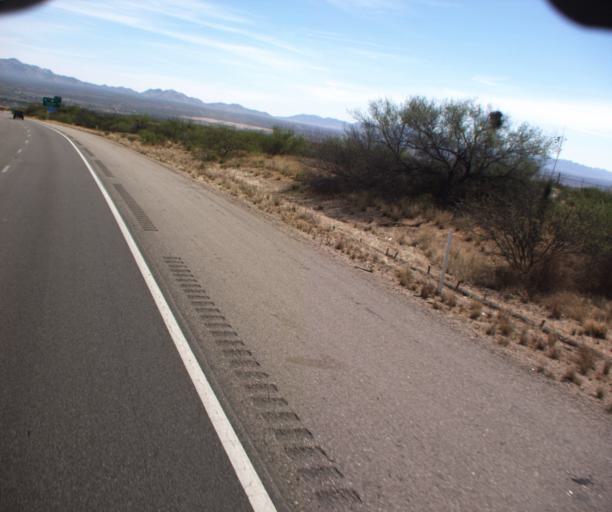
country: US
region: Arizona
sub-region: Cochise County
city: Whetstone
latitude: 31.9680
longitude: -110.3332
